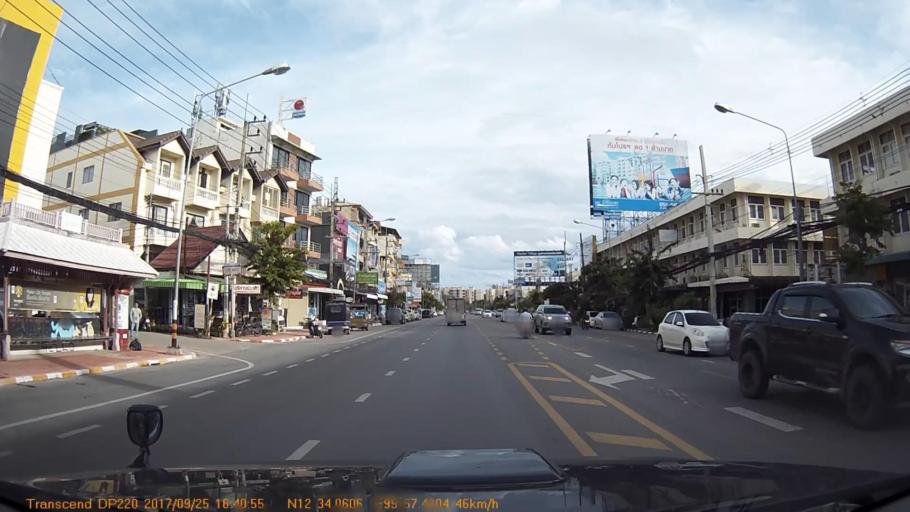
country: TH
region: Prachuap Khiri Khan
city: Hua Hin
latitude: 12.5677
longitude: 99.9580
